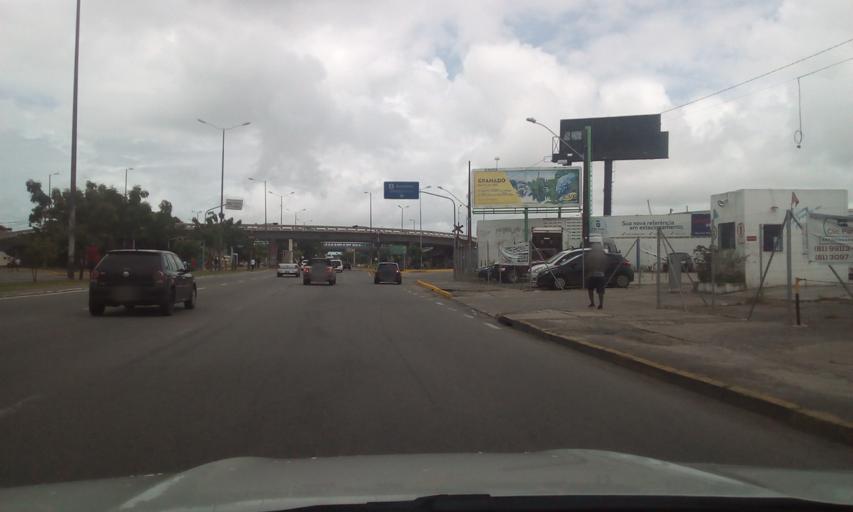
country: BR
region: Pernambuco
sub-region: Recife
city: Recife
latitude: -8.1287
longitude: -34.9159
